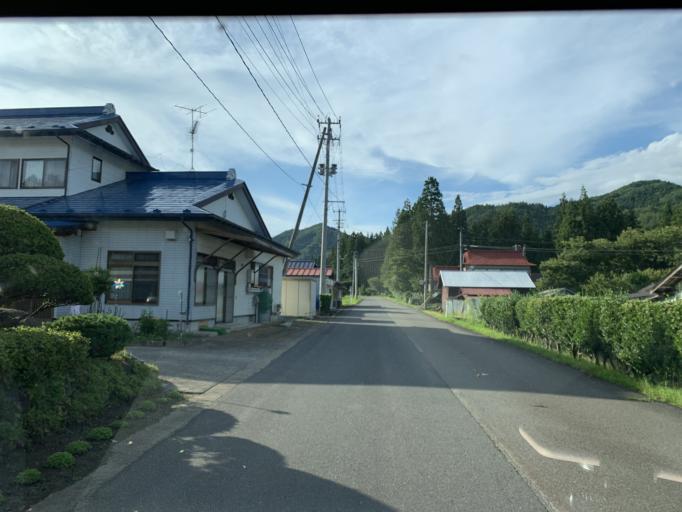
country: JP
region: Iwate
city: Ichinoseki
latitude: 38.8949
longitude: 140.9410
